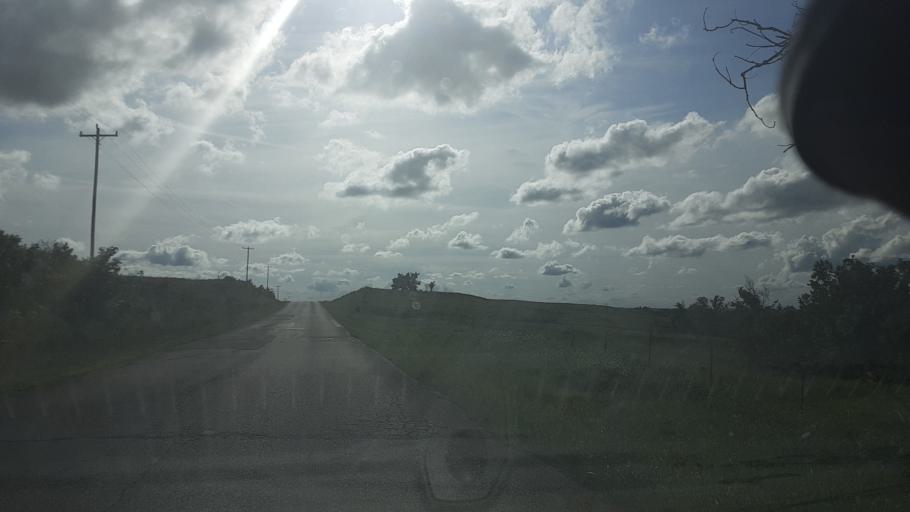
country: US
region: Oklahoma
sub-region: Logan County
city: Langston
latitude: 36.0579
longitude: -97.3604
